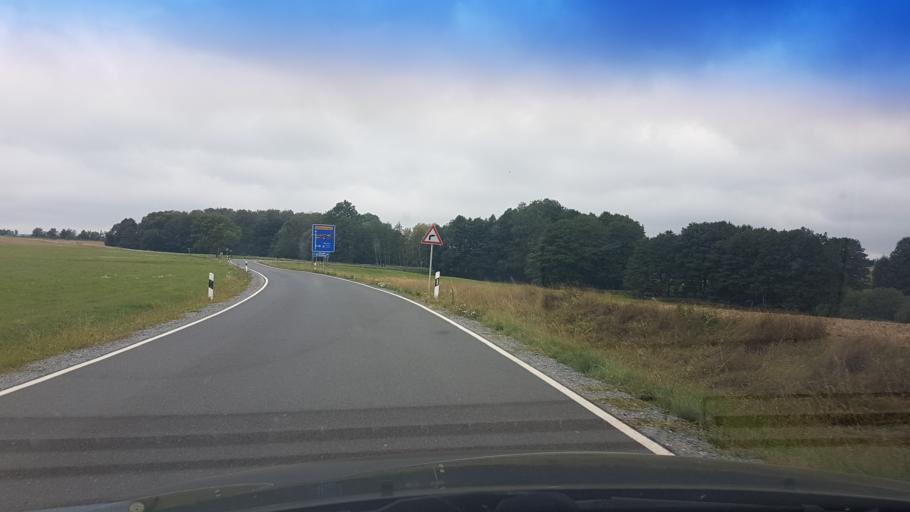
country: DE
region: Bavaria
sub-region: Upper Franconia
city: Marktschorgast
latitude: 50.0787
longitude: 11.6696
